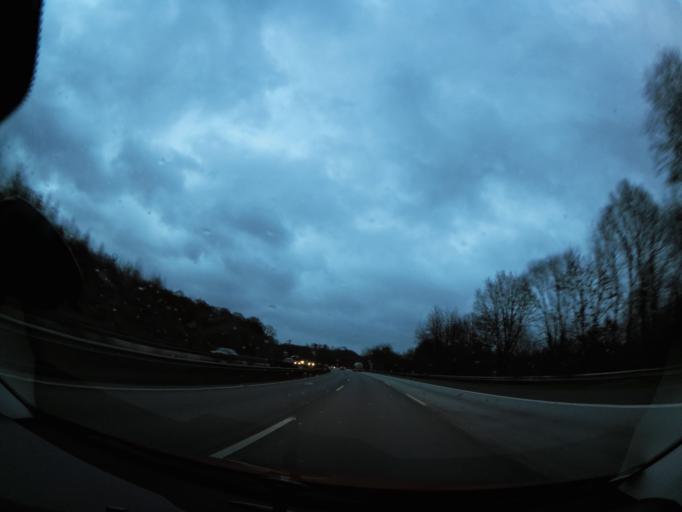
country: DE
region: Rheinland-Pfalz
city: Eppenrod
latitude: 50.4144
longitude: 7.9314
